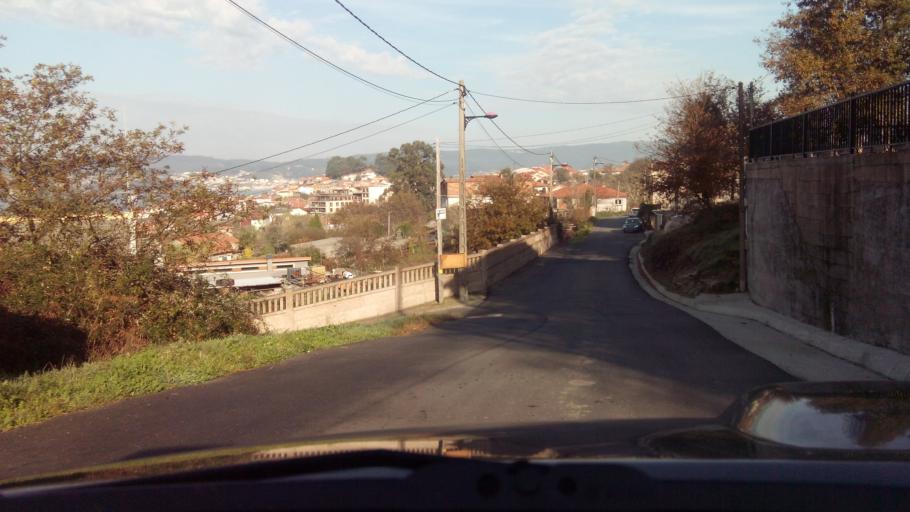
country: ES
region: Galicia
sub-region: Provincia de Pontevedra
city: Marin
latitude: 42.3609
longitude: -8.7340
